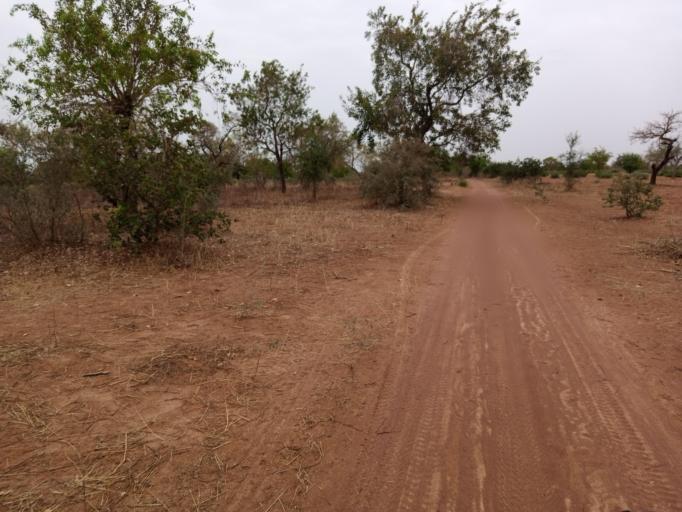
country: BF
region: Boucle du Mouhoun
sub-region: Province de la Kossi
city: Nouna
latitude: 12.8383
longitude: -4.0769
